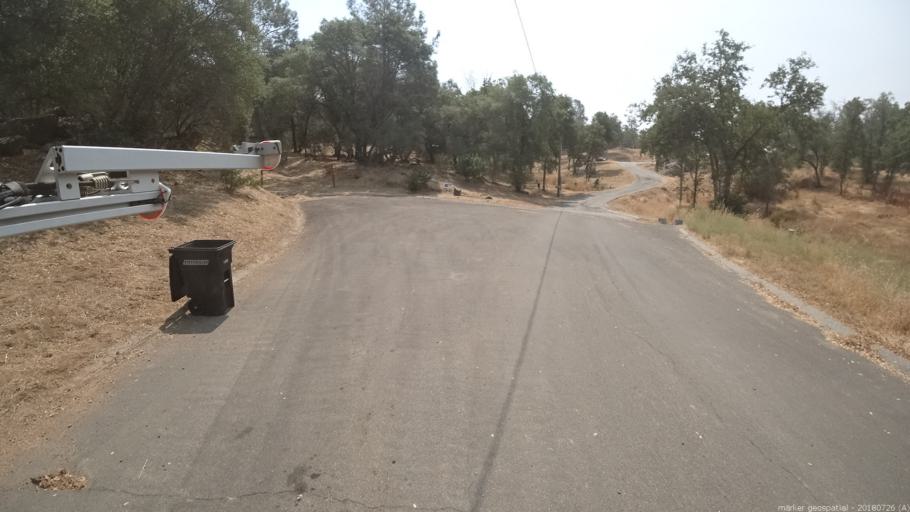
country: US
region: California
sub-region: Madera County
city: Coarsegold
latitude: 37.2472
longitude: -119.6830
